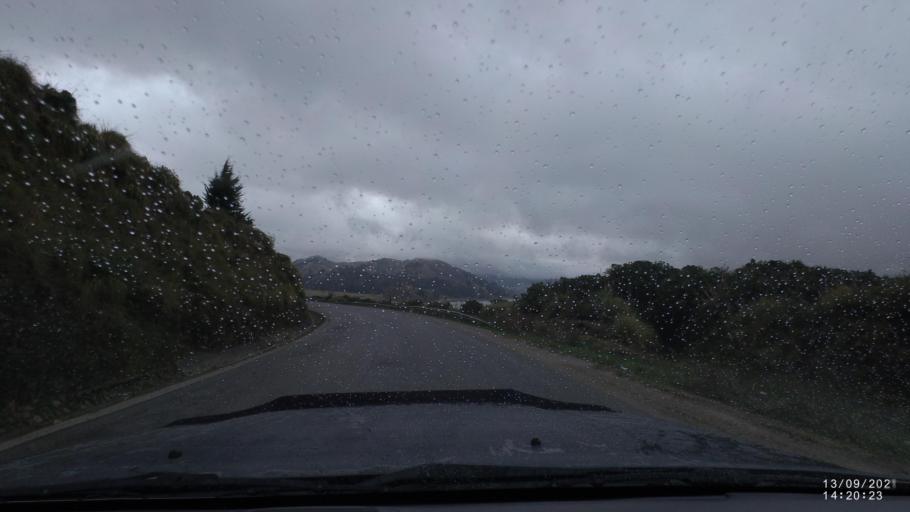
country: BO
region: Cochabamba
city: Colomi
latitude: -17.2516
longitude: -65.8952
